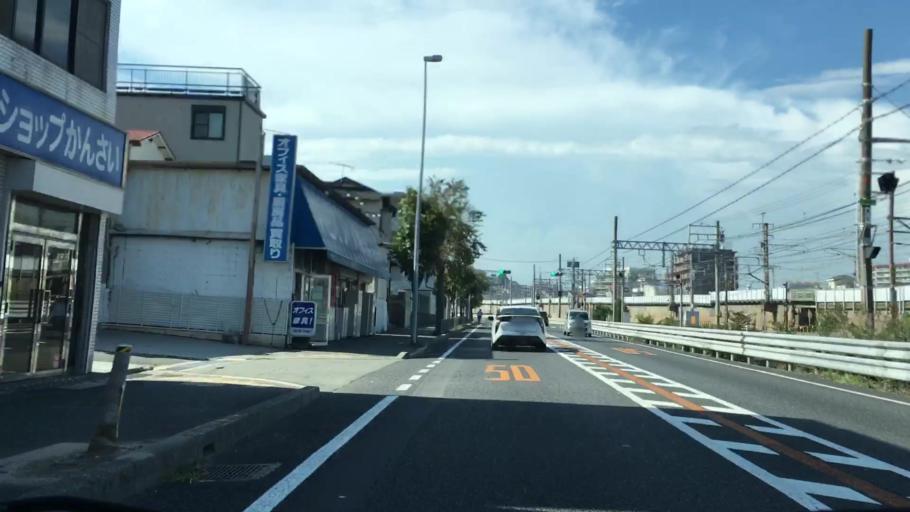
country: JP
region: Hyogo
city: Akashi
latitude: 34.6362
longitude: 135.0304
